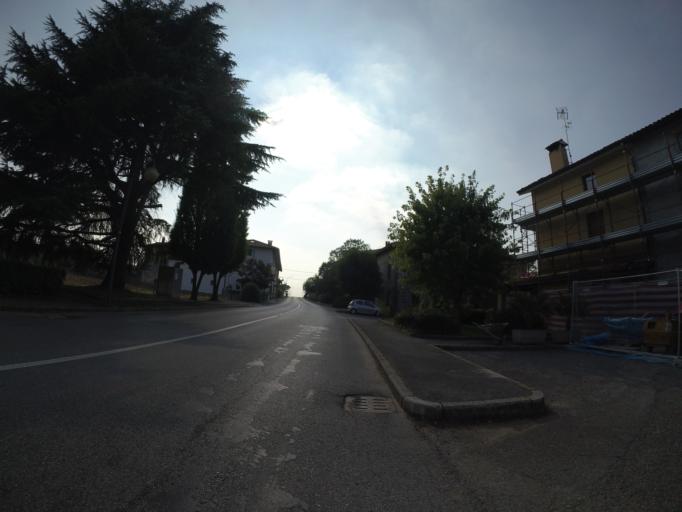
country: IT
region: Friuli Venezia Giulia
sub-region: Provincia di Udine
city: Basiliano
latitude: 45.9959
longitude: 13.0240
